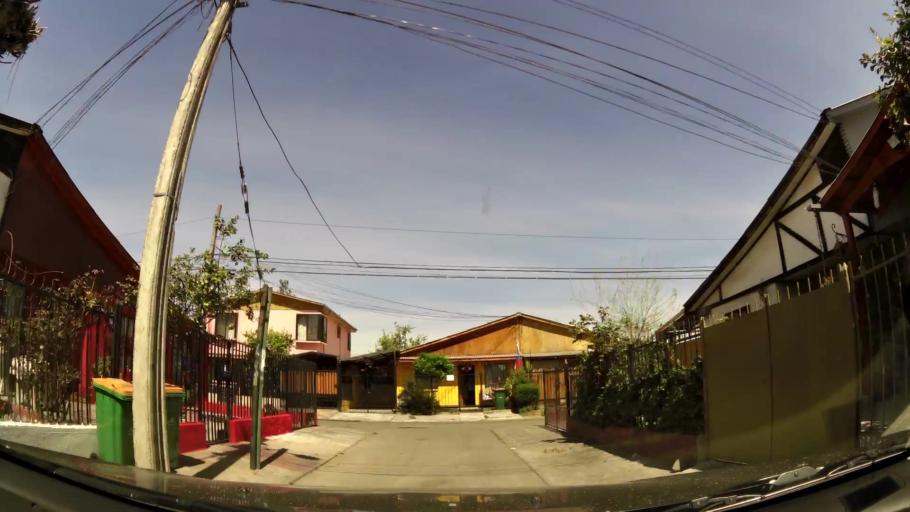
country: CL
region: Santiago Metropolitan
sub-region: Provincia de Cordillera
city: Puente Alto
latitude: -33.5727
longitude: -70.5724
